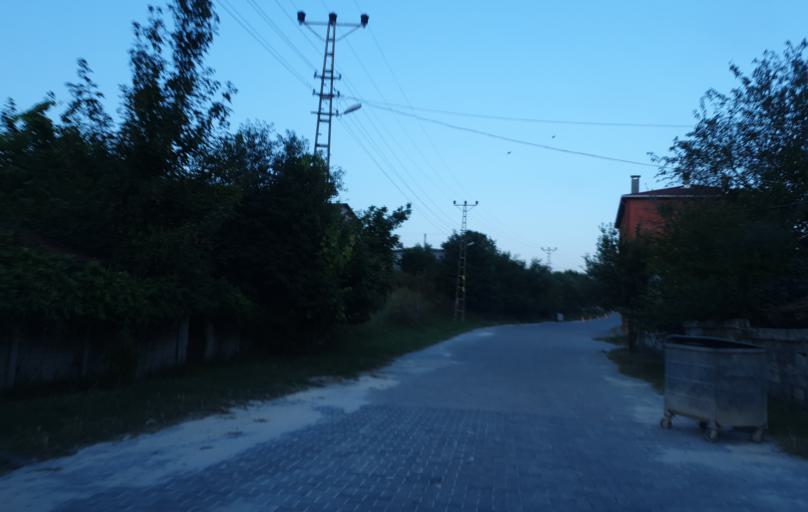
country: TR
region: Tekirdag
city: Velimese
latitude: 41.3504
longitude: 27.8798
